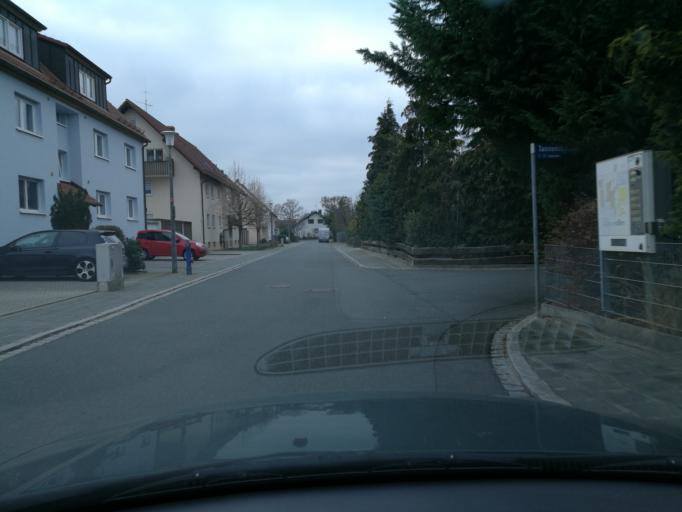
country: DE
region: Bavaria
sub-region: Regierungsbezirk Mittelfranken
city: Seukendorf
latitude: 49.4883
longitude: 10.8835
